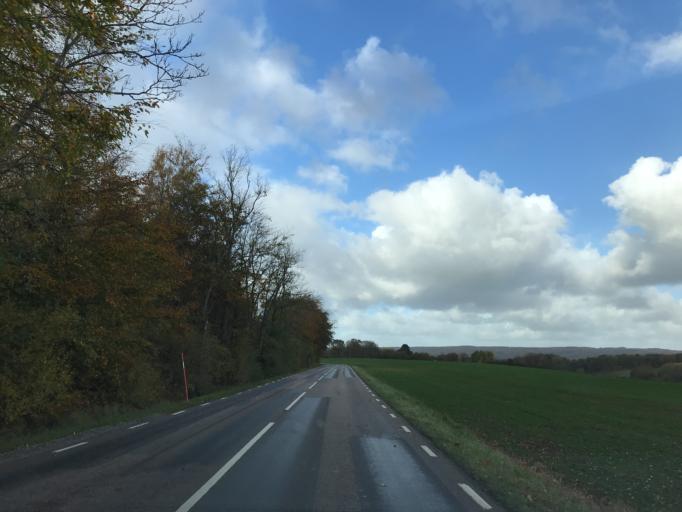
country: SE
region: Skane
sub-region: Svalovs Kommun
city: Kagerod
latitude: 56.0223
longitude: 13.0469
